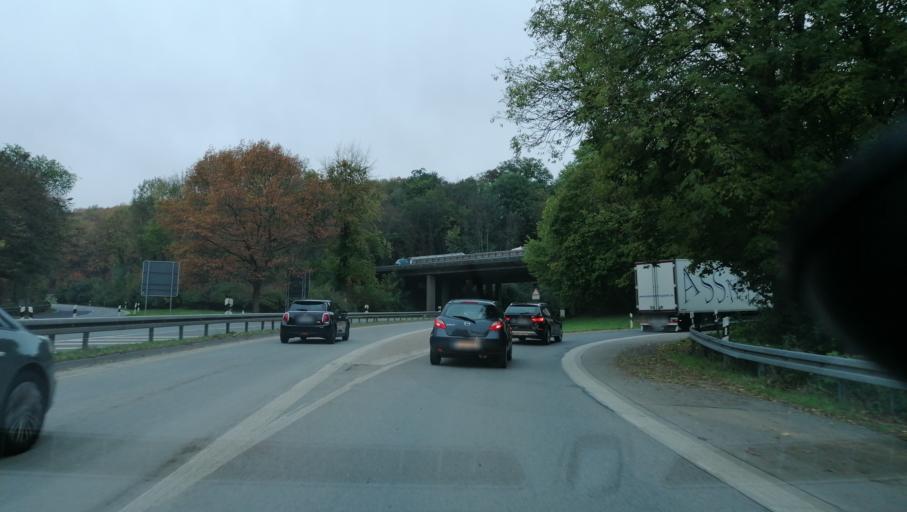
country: DE
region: North Rhine-Westphalia
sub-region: Regierungsbezirk Dusseldorf
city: Wuppertal
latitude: 51.2794
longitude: 7.1815
